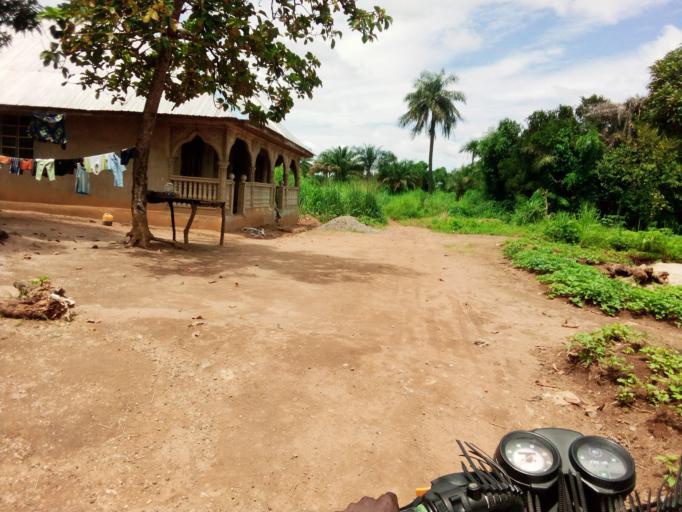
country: SL
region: Eastern Province
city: Koidu
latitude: 8.6455
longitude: -10.9250
